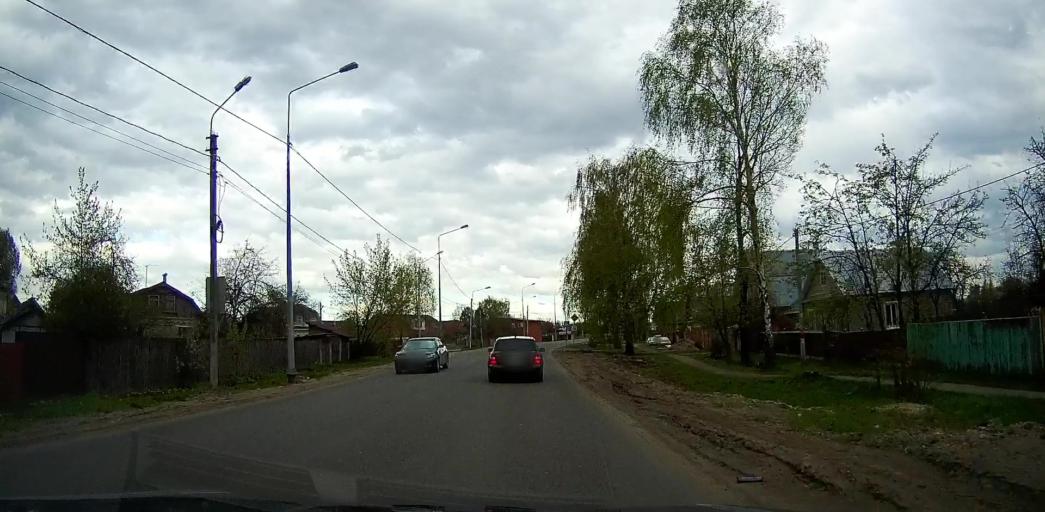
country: RU
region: Moskovskaya
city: Pavlovskiy Posad
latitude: 55.7707
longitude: 38.6931
